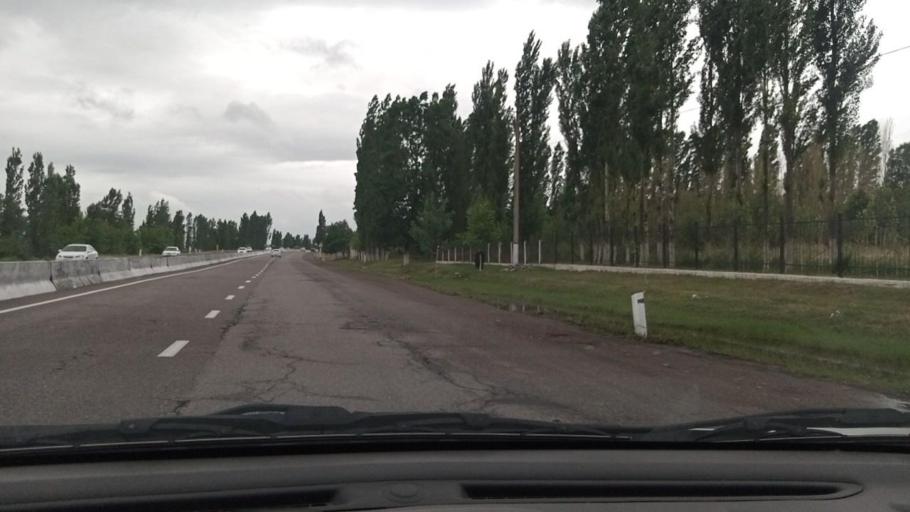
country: UZ
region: Toshkent
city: Angren
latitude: 40.9673
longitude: 69.9715
